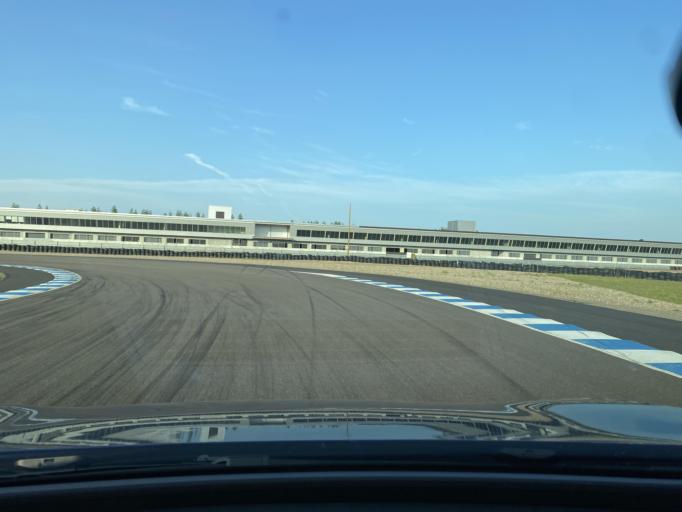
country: FI
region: Kymenlaakso
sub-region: Kouvola
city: Iitti
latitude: 60.8812
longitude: 26.4830
